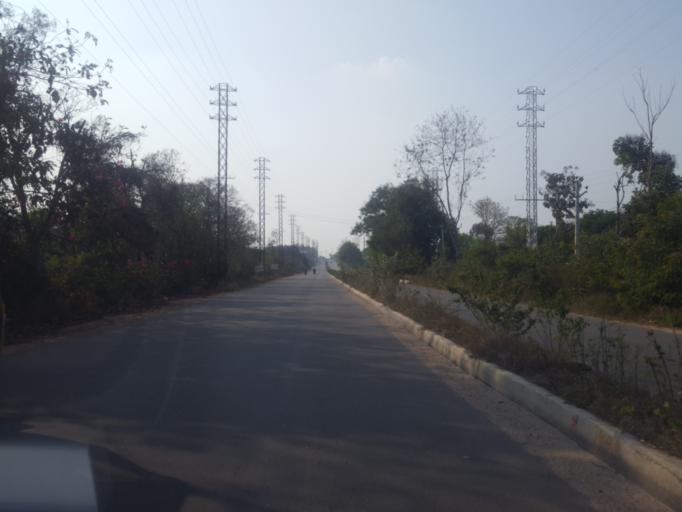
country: IN
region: Telangana
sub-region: Medak
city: Serilingampalle
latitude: 17.4166
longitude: 78.2561
